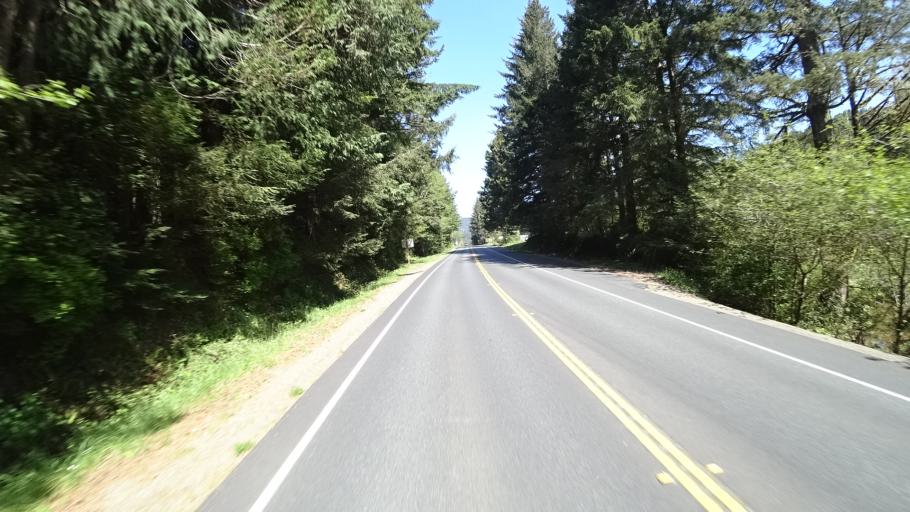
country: US
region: California
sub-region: Del Norte County
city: Bertsch-Oceanview
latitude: 41.5652
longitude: -124.0674
